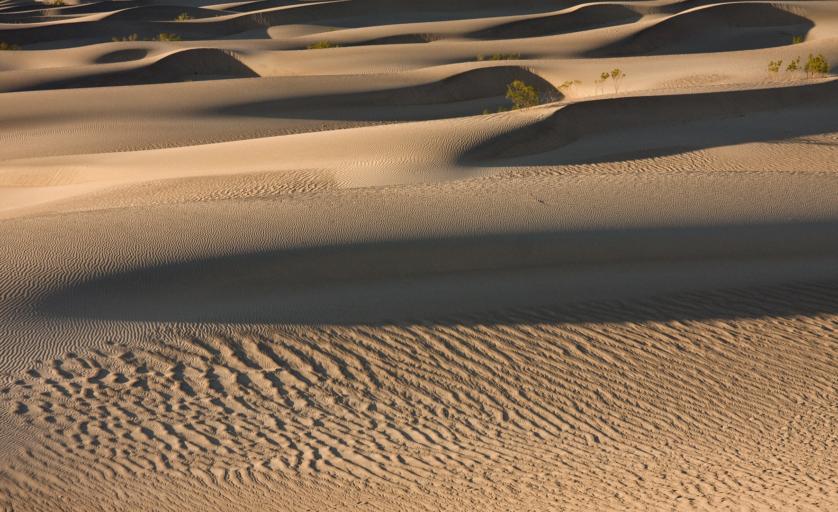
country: US
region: Nevada
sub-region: Nye County
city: Beatty
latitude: 36.6152
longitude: -117.1129
